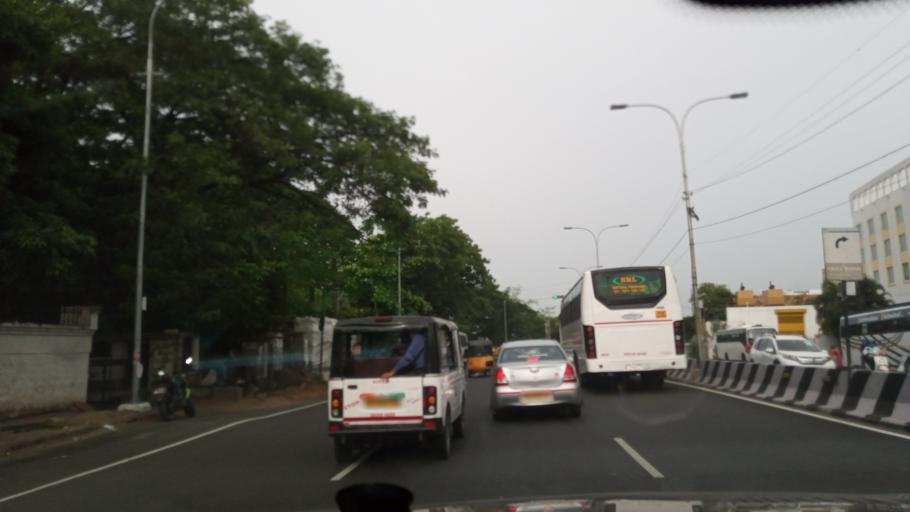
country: IN
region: Tamil Nadu
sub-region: Kancheepuram
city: Manappakkam
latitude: 13.0207
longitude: 80.1845
